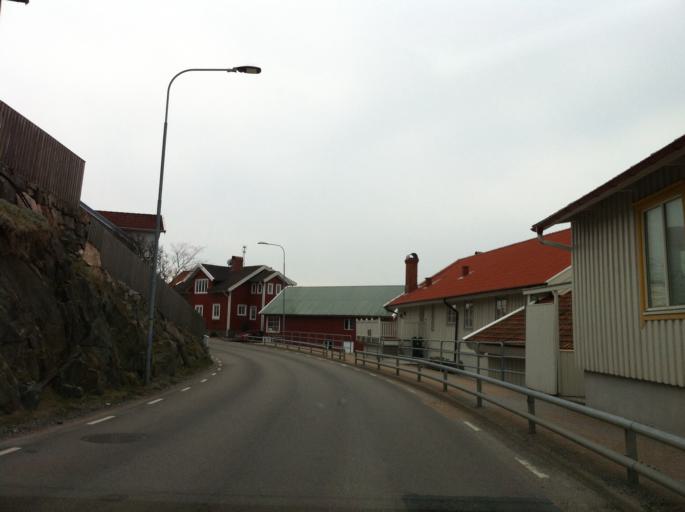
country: SE
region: Vaestra Goetaland
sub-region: Orust
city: Henan
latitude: 58.1651
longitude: 11.7046
